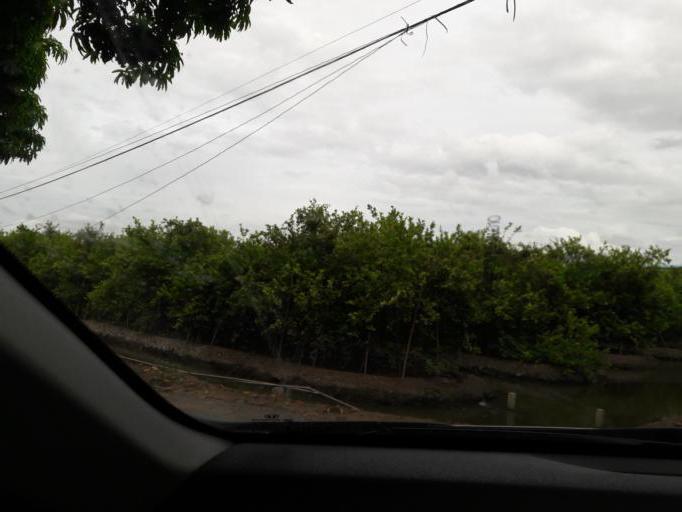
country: TH
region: Ratchaburi
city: Damnoen Saduak
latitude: 13.5448
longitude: 99.9789
